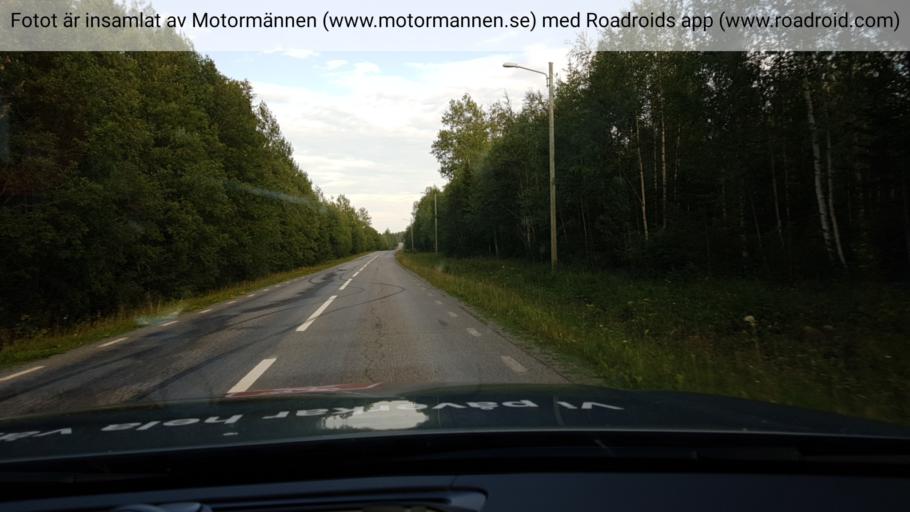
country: SE
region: Jaemtland
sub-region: Krokoms Kommun
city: Krokom
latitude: 63.1602
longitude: 14.1328
